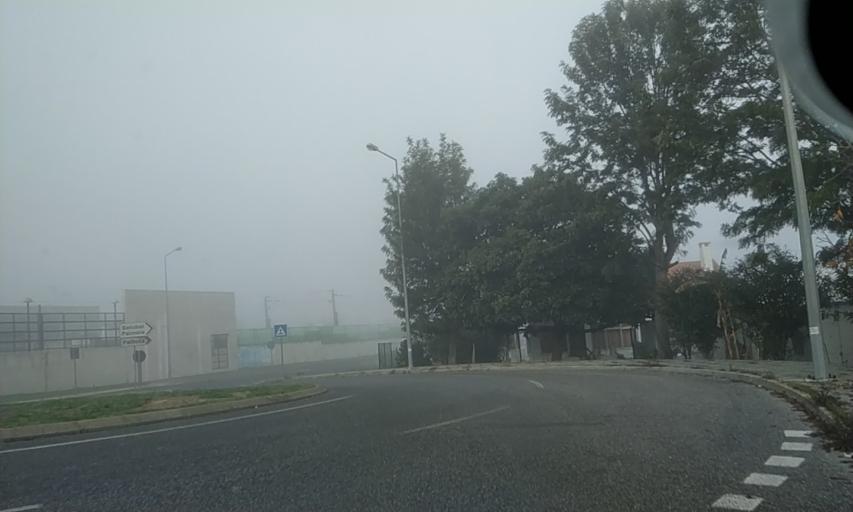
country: PT
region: Setubal
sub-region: Palmela
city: Pinhal Novo
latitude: 38.6071
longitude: -8.8885
